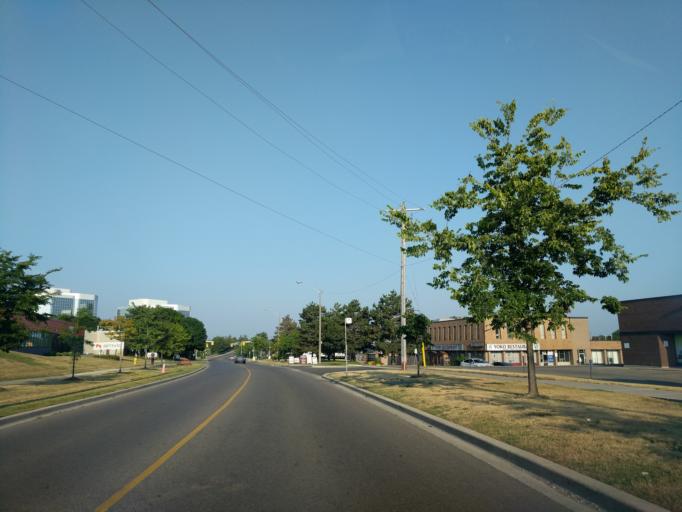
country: CA
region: Ontario
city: Willowdale
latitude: 43.8039
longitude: -79.3395
